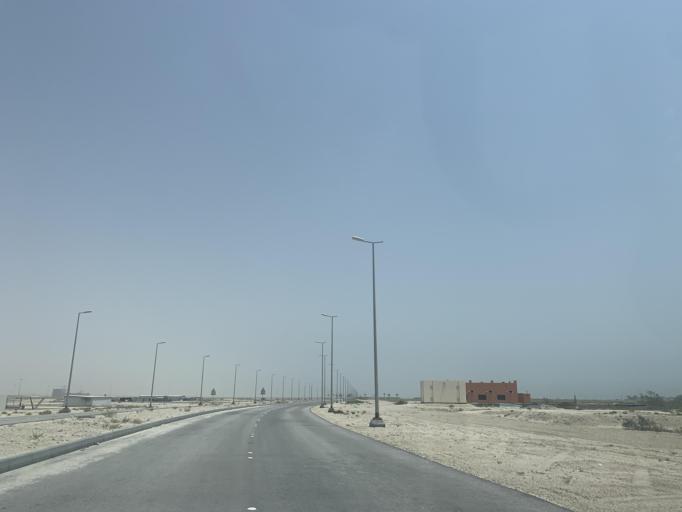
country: BH
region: Central Governorate
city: Dar Kulayb
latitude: 25.8401
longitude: 50.5877
